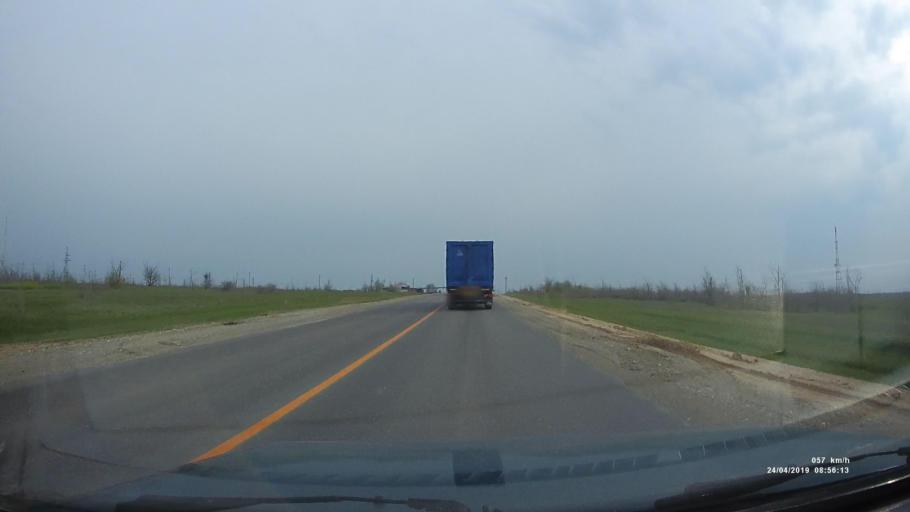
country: RU
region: Kalmykiya
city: Arshan'
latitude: 46.3002
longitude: 44.1831
